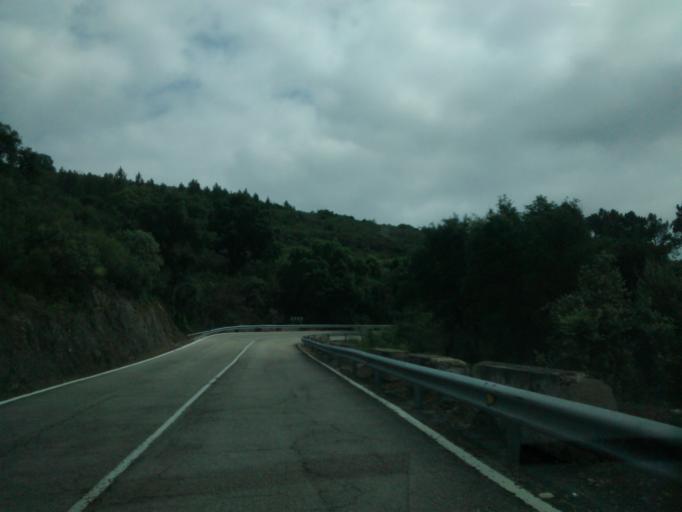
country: ES
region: Galicia
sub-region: Provincia de Ourense
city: Manzaneda
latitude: 42.3367
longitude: -7.1857
